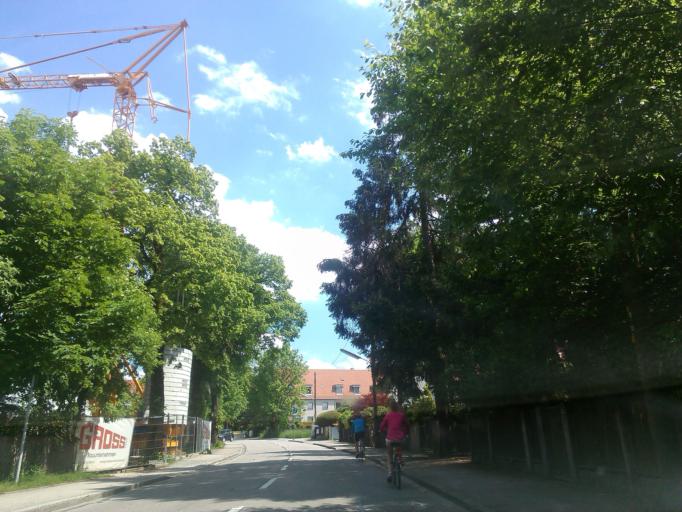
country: DE
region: Bavaria
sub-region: Upper Bavaria
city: Pullach im Isartal
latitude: 48.0770
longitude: 11.5111
